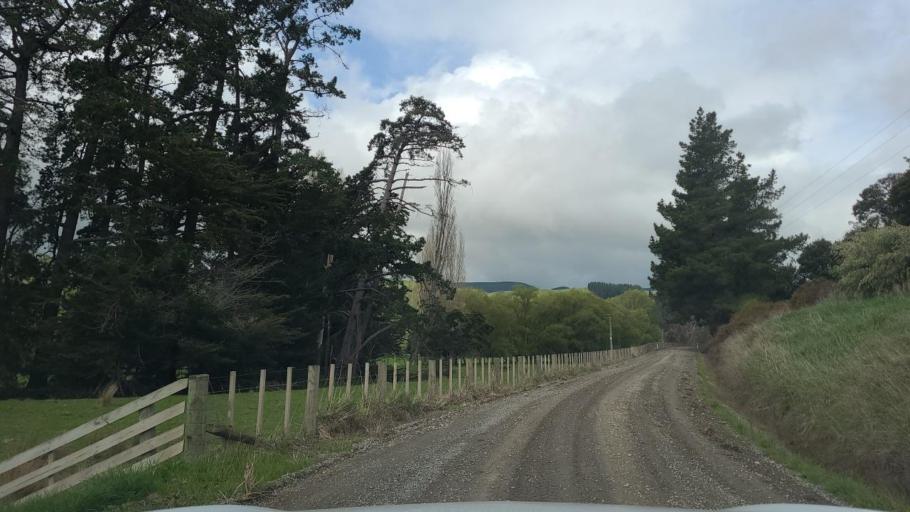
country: NZ
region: Wellington
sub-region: Masterton District
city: Masterton
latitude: -41.1561
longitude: 175.6095
